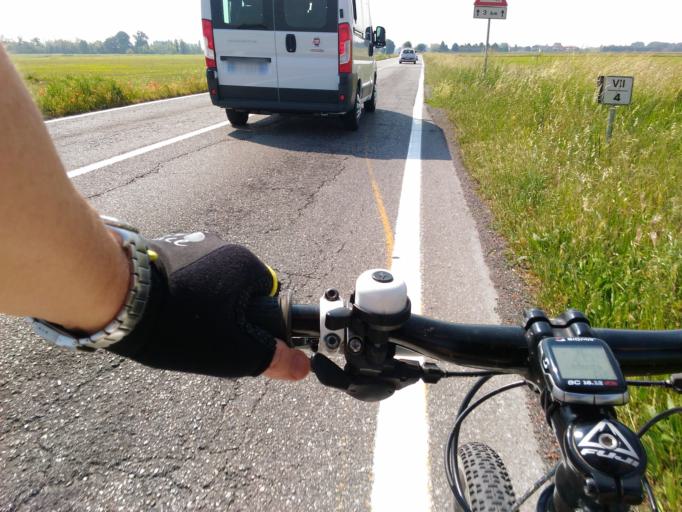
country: IT
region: Lombardy
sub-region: Provincia di Lodi
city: Salerano sul Lambro
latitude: 45.2818
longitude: 9.3807
